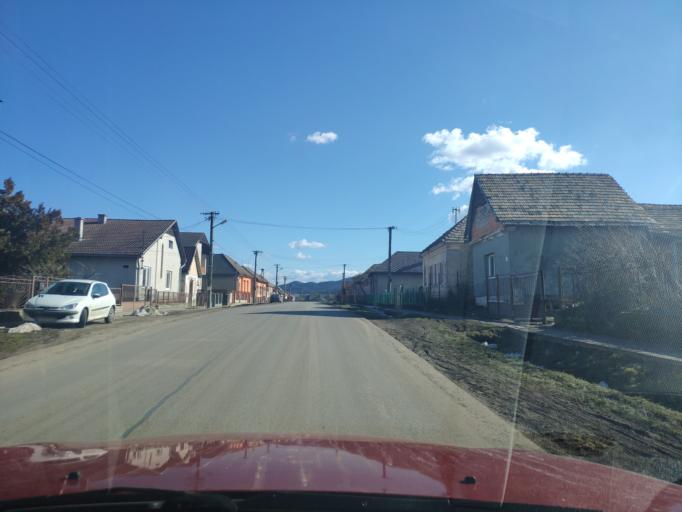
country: SK
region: Banskobystricky
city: Rimavska Sobota
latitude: 48.2879
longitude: 20.0903
